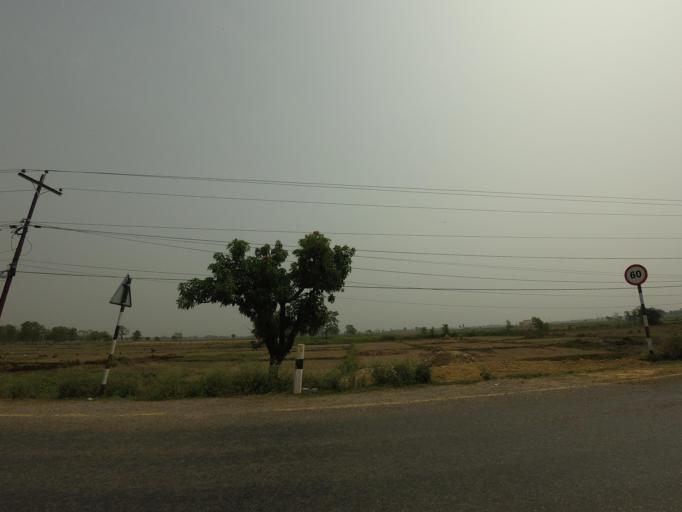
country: IN
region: Uttar Pradesh
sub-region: Maharajganj
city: Nautanwa
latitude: 27.4911
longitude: 83.2929
